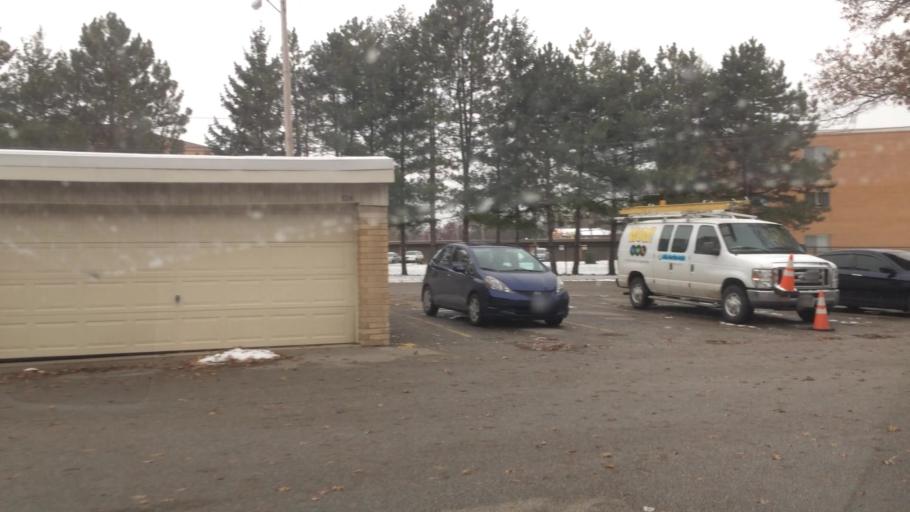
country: US
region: Ohio
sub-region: Cuyahoga County
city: Middleburg Heights
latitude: 41.3422
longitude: -81.8247
